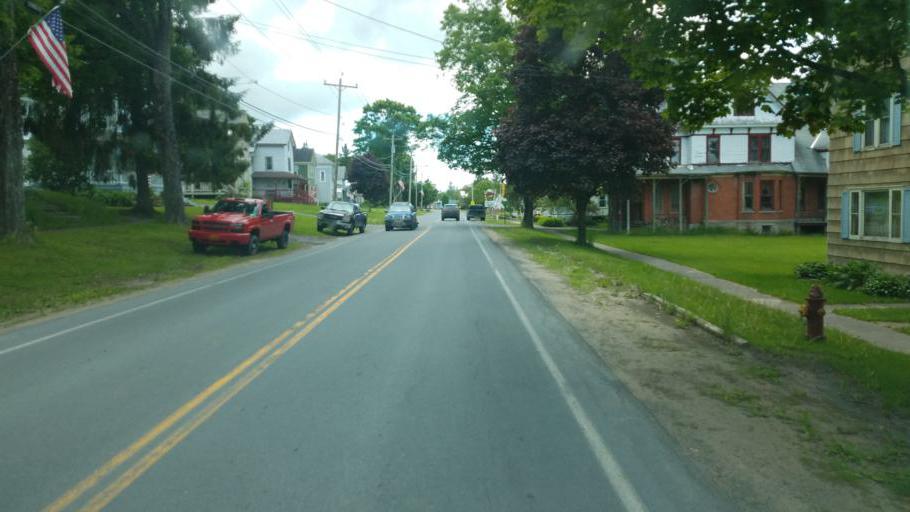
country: US
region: New York
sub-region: Oneida County
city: Boonville
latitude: 43.3298
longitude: -75.1874
